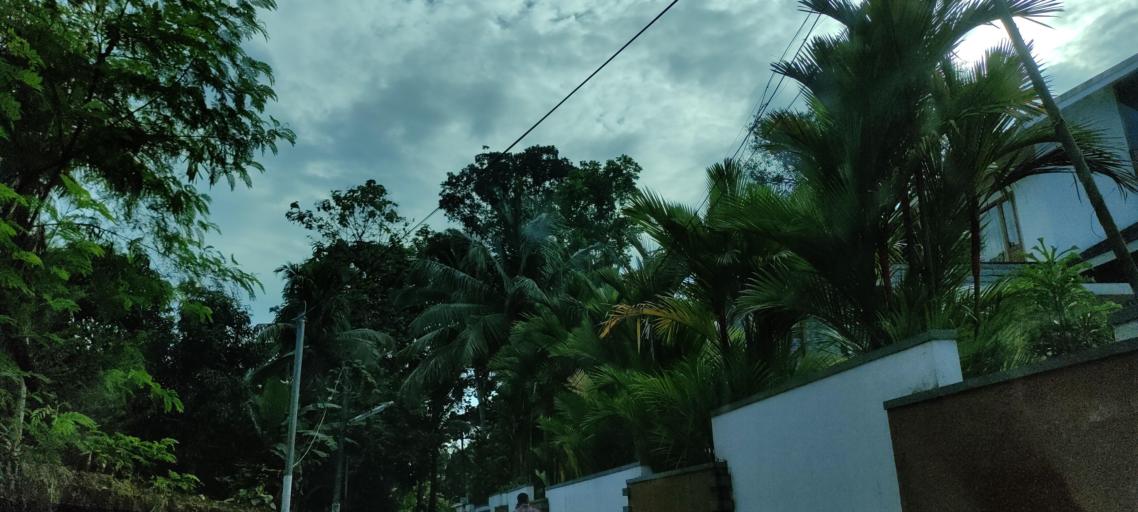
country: IN
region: Kerala
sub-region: Alappuzha
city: Mavelikara
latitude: 9.2515
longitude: 76.5448
